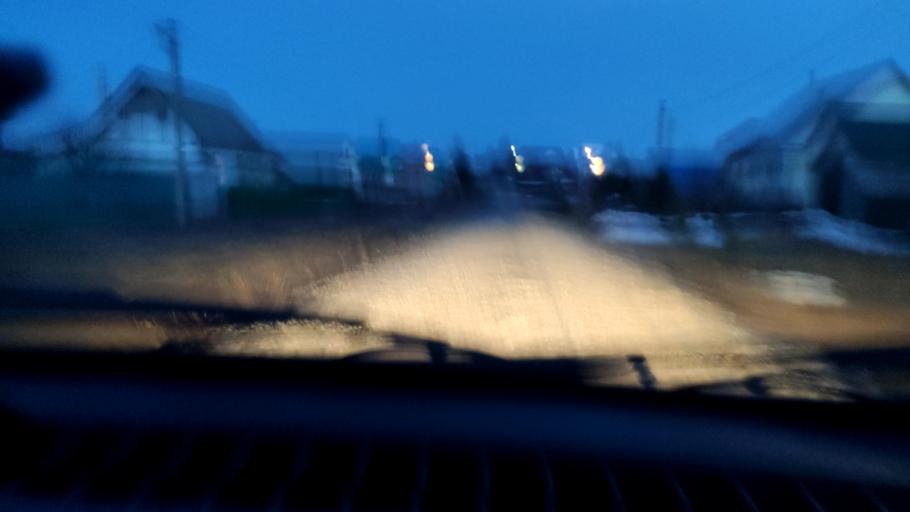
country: RU
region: Bashkortostan
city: Iglino
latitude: 54.7925
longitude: 56.3129
